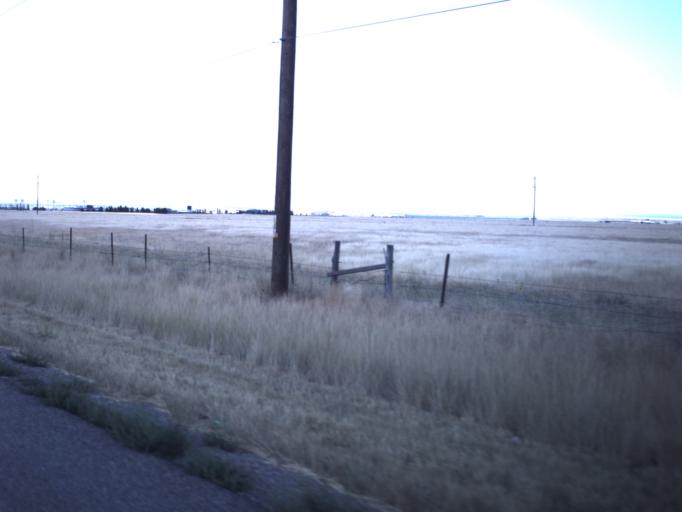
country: US
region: Utah
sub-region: Tooele County
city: Tooele
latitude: 40.5631
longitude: -112.3589
